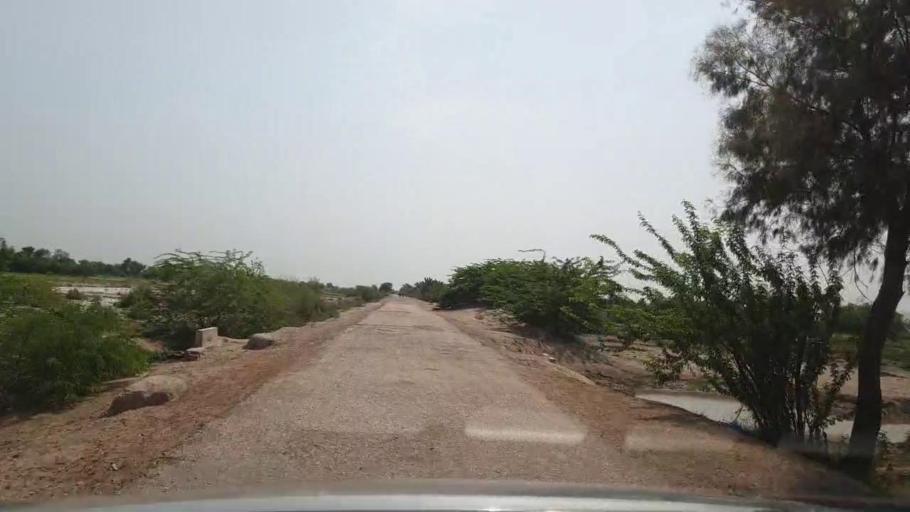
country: PK
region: Sindh
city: Pano Aqil
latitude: 27.6169
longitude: 69.1355
